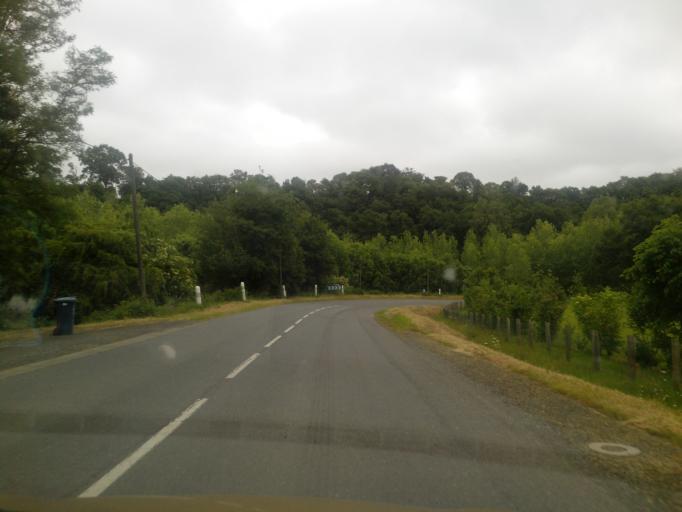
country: FR
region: Brittany
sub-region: Departement d'Ille-et-Vilaine
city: Sens-de-Bretagne
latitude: 48.3444
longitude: -1.4818
